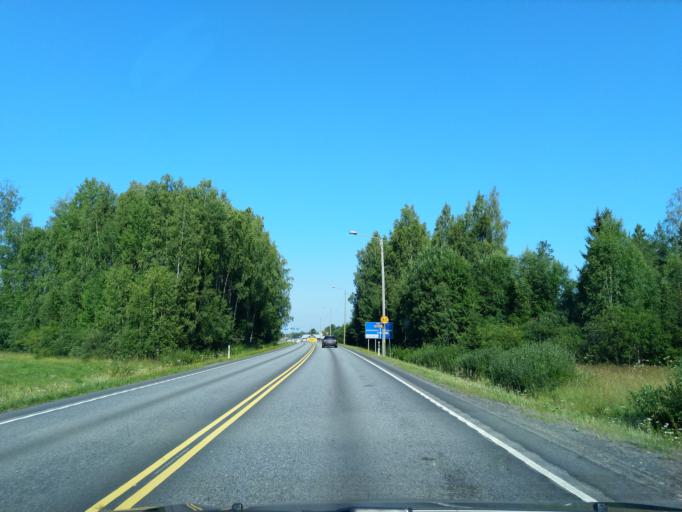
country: FI
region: Satakunta
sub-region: Pori
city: Huittinen
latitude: 61.1646
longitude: 22.7124
